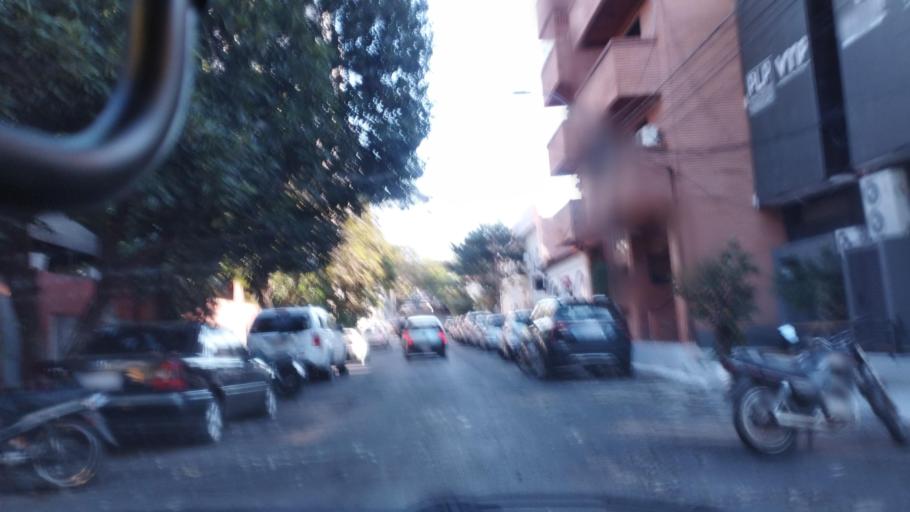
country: PY
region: Asuncion
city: Asuncion
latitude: -25.2941
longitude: -57.6138
